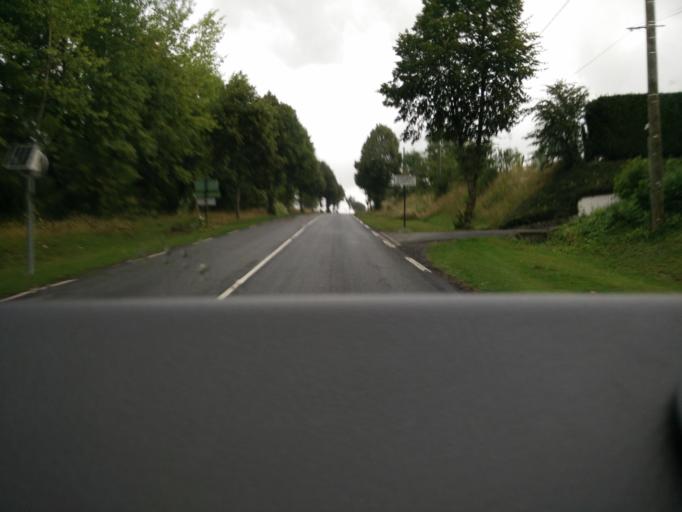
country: FR
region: Nord-Pas-de-Calais
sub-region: Departement du Pas-de-Calais
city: Aubigny-en-Artois
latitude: 50.3564
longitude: 2.5918
